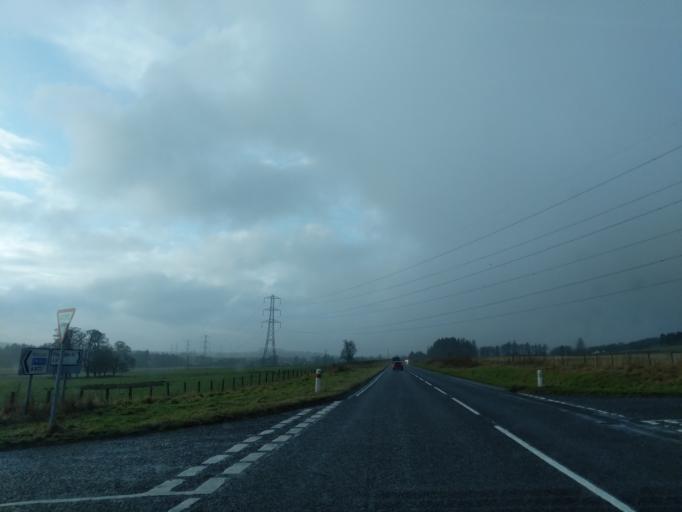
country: GB
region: Scotland
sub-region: Fife
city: Saline
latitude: 56.1930
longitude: -3.5255
